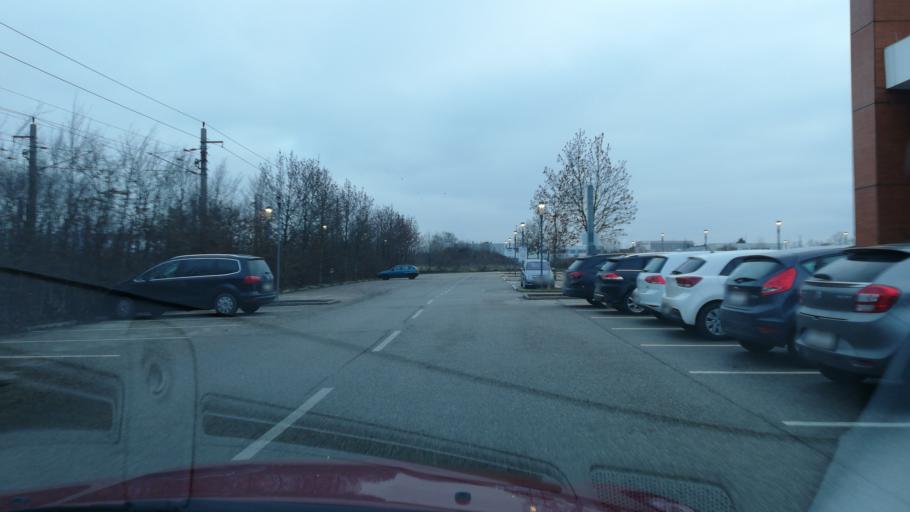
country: AT
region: Upper Austria
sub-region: Wels Stadt
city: Wels
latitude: 48.1816
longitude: 14.0621
